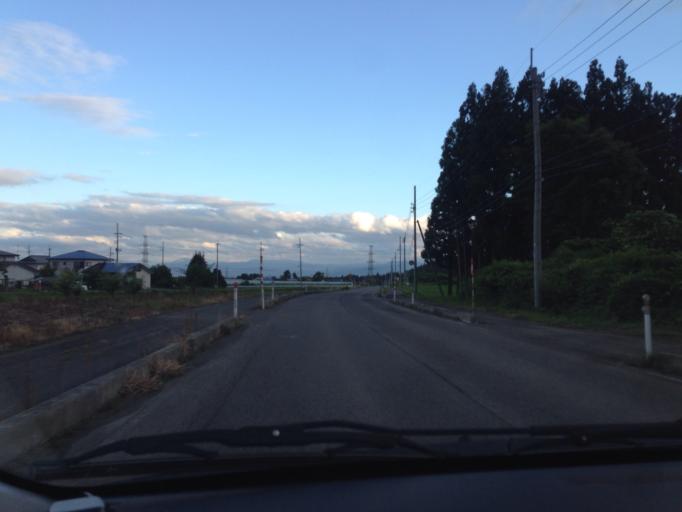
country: JP
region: Fukushima
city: Kitakata
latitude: 37.7166
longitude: 139.8712
